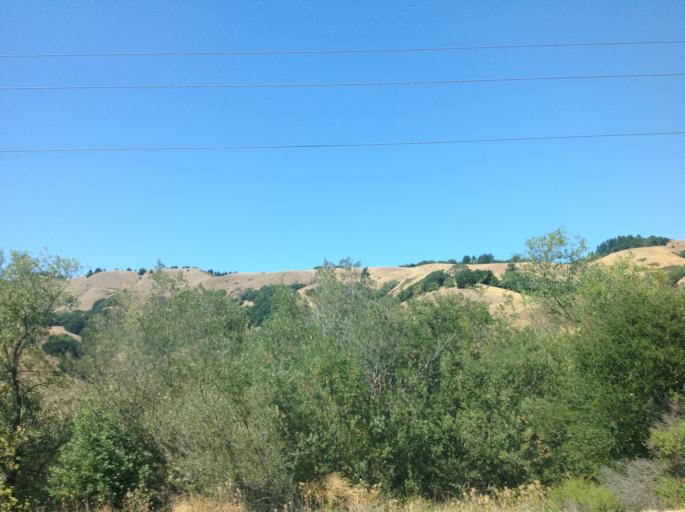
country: US
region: California
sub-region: Marin County
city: Woodacre
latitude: 38.0160
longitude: -122.6394
